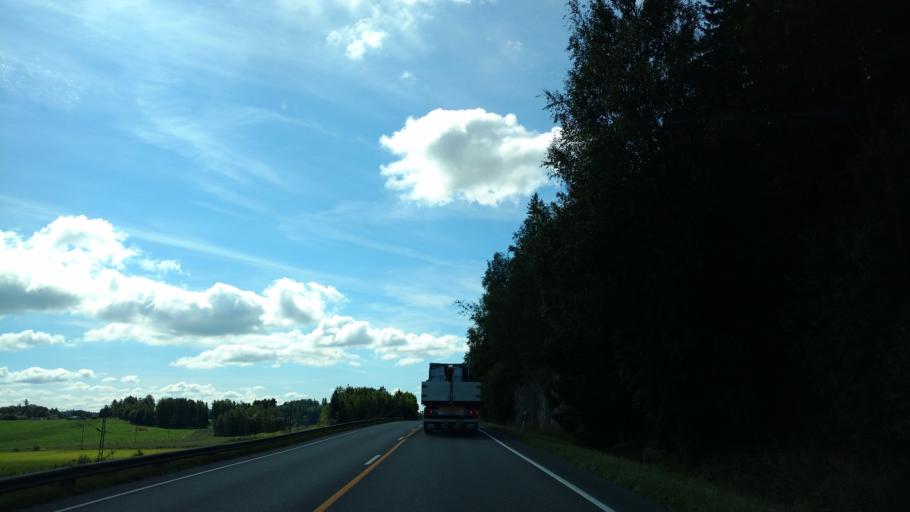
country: FI
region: Varsinais-Suomi
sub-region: Salo
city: Pernioe
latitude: 60.2846
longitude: 23.1155
